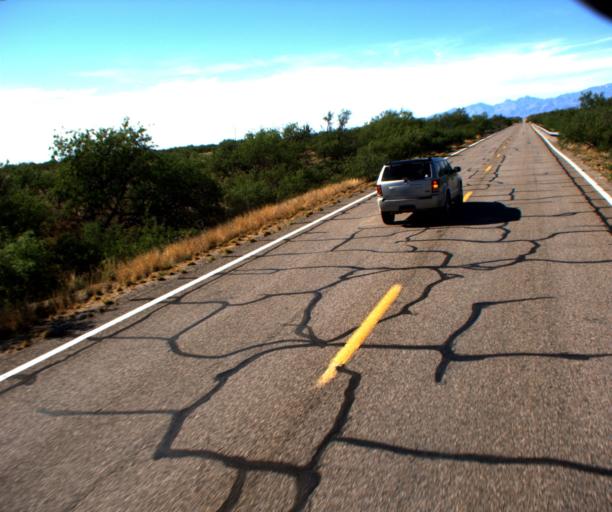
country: US
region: Arizona
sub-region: Pima County
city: Vail
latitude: 31.9588
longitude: -110.6702
